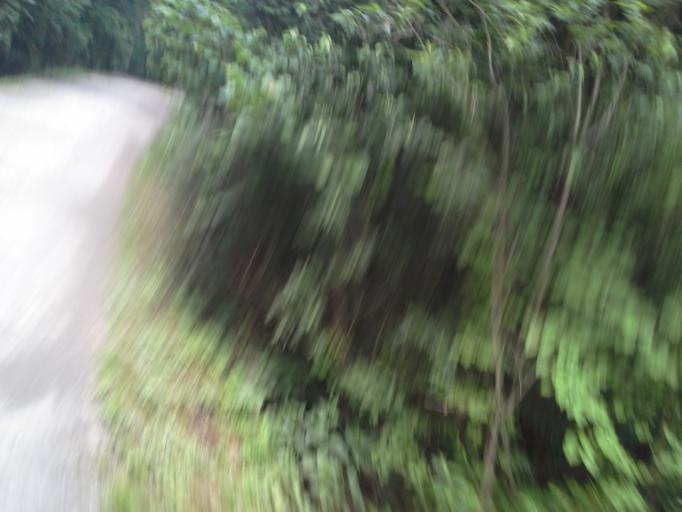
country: RU
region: Moskovskaya
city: Kievskij
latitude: 55.4372
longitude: 36.8368
